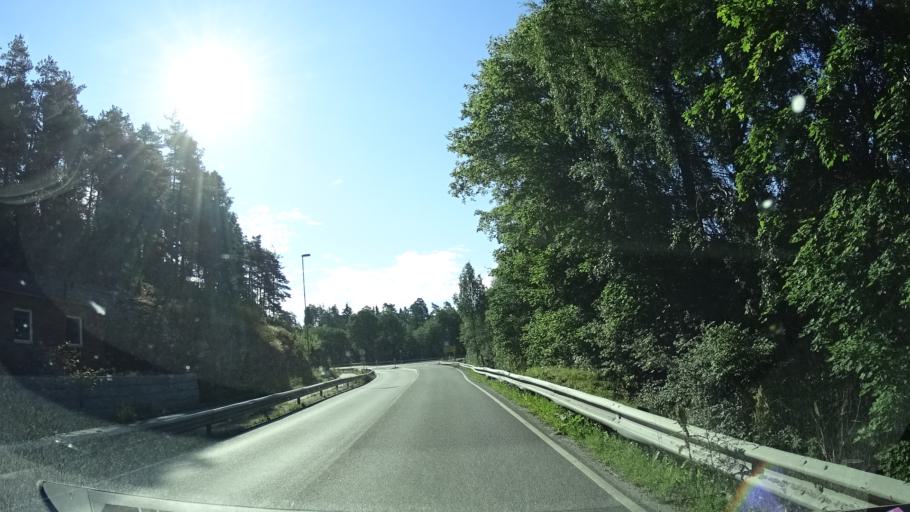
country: NO
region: Ostfold
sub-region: Eidsberg
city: Mysen
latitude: 59.5493
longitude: 11.3471
